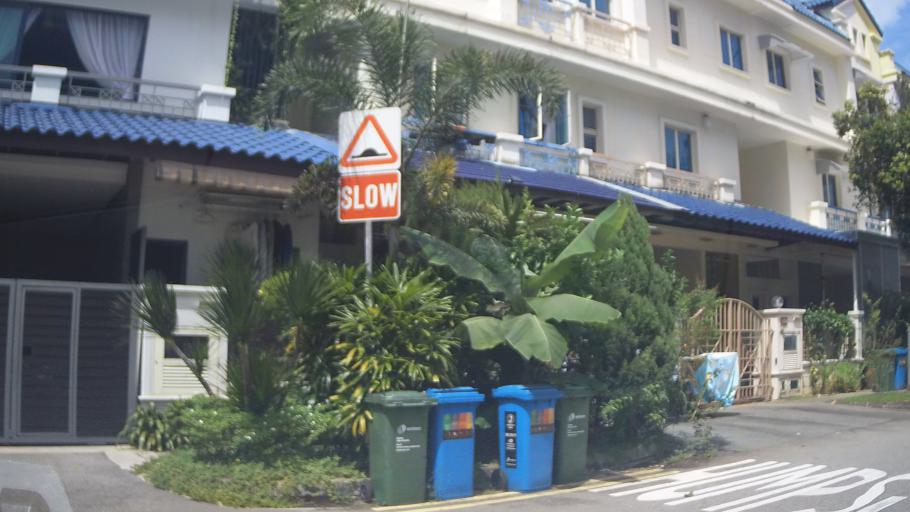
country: MY
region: Johor
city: Johor Bahru
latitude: 1.3920
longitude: 103.7500
